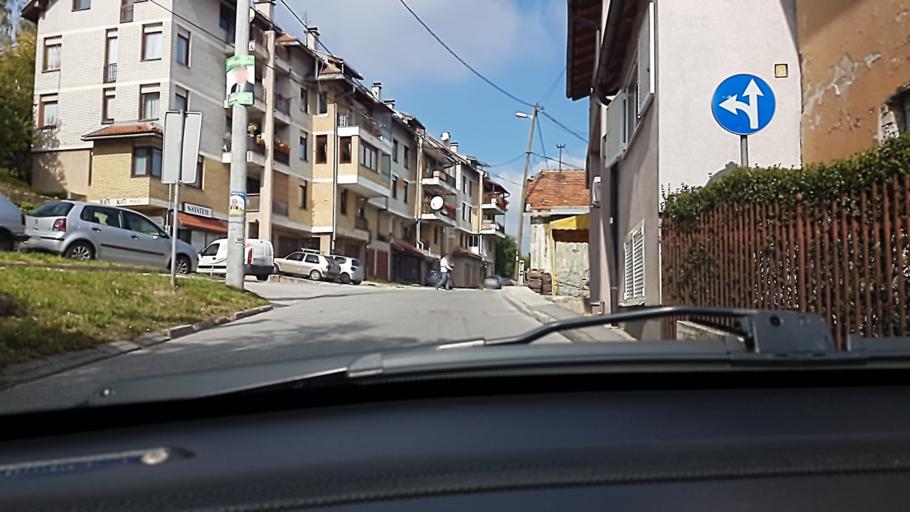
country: BA
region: Federation of Bosnia and Herzegovina
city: Kobilja Glava
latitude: 43.8612
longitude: 18.4088
